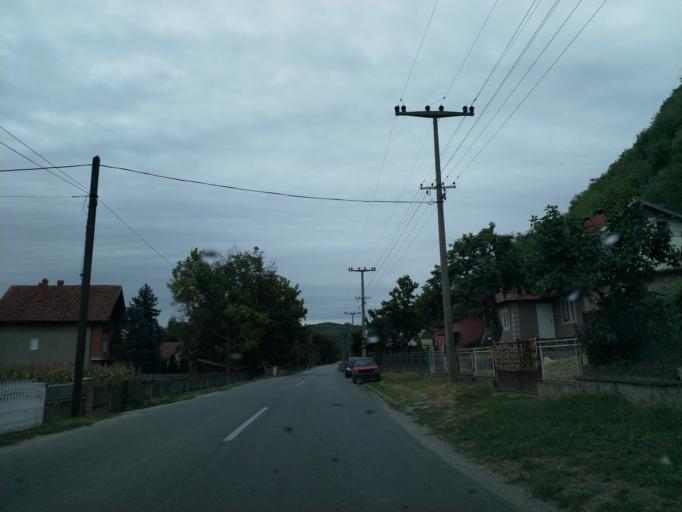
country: RS
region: Central Serbia
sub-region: Sumadijski Okrug
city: Batocina
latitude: 44.1025
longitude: 21.1626
